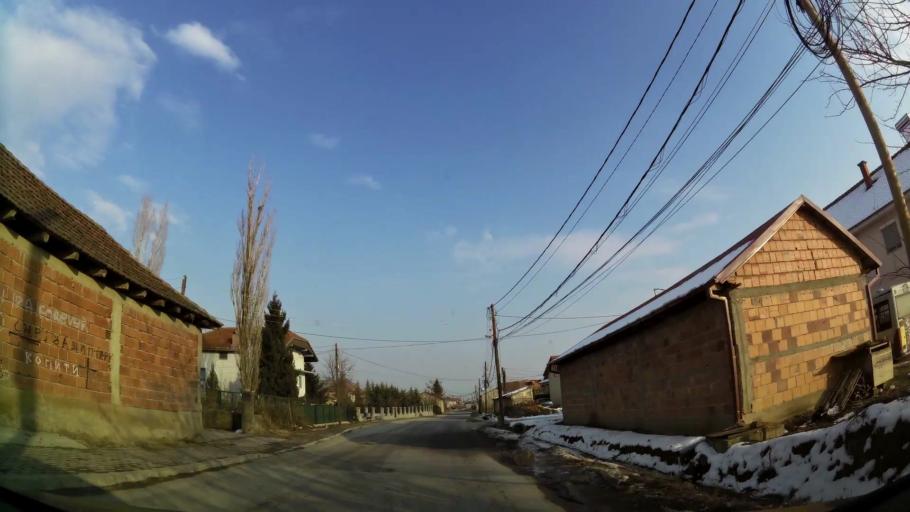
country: MK
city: Creshevo
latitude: 42.0277
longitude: 21.5193
